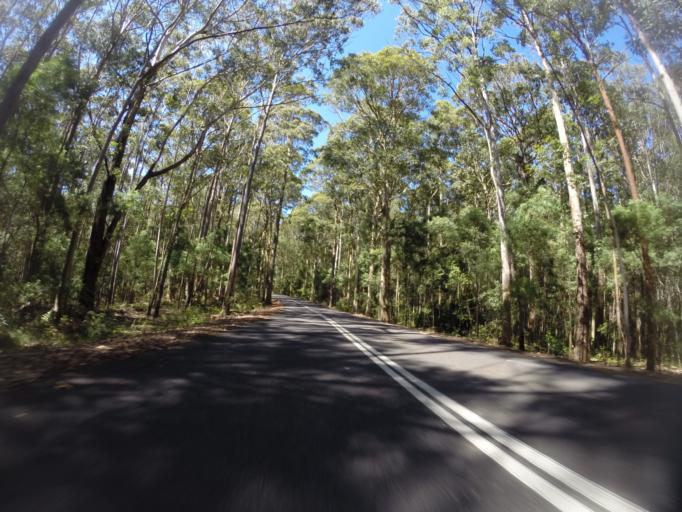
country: AU
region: New South Wales
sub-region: Eurobodalla
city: Batemans Bay
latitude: -35.6569
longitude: 150.2621
